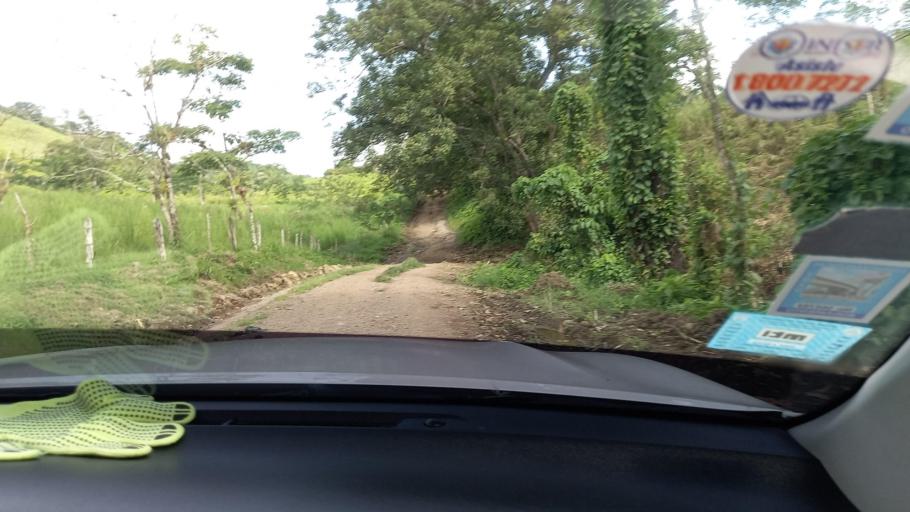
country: NI
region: Jinotega
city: San Jose de Bocay
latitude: 13.3939
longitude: -85.6944
